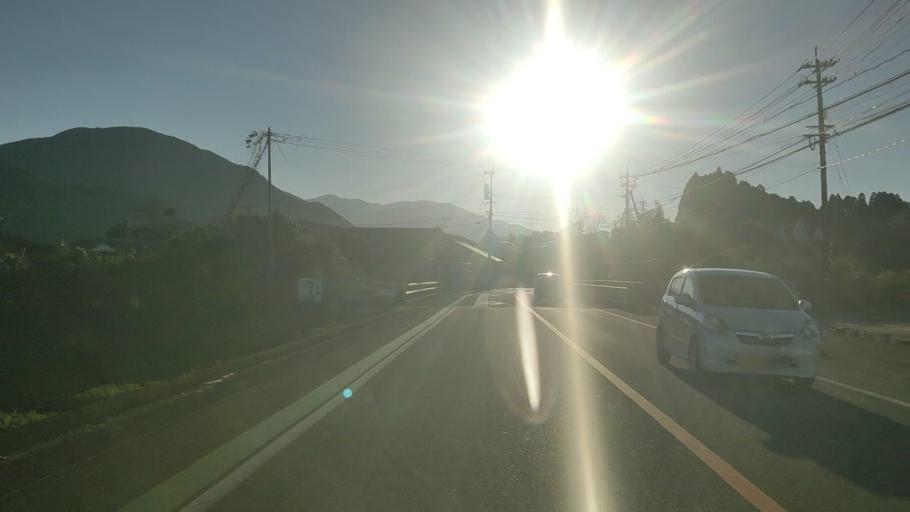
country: JP
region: Miyazaki
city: Miyazaki-shi
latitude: 31.8389
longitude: 131.3352
